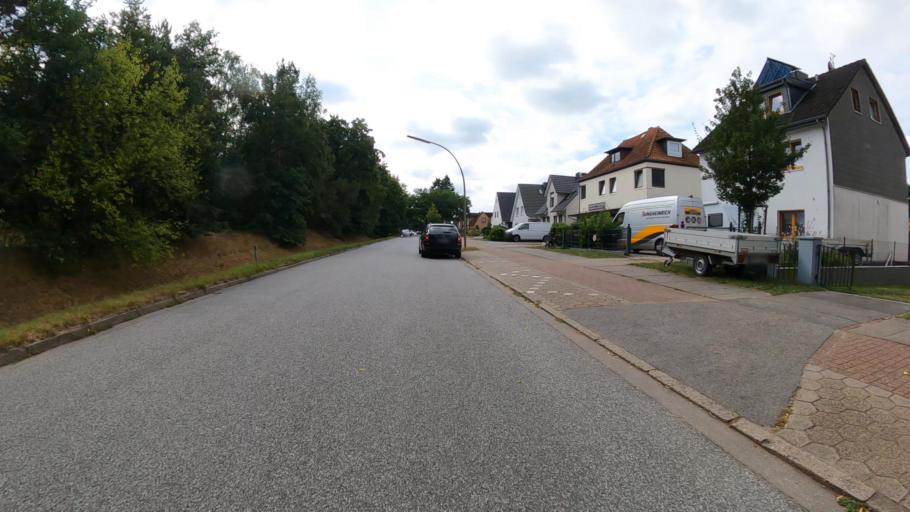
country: DE
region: Lower Saxony
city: Neu Wulmstorf
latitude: 53.4635
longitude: 9.8660
